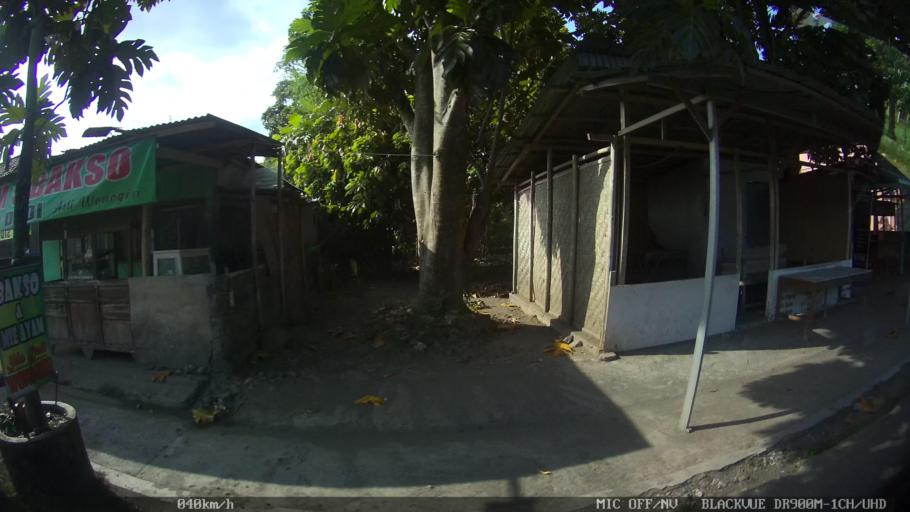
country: ID
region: Central Java
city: Candi Prambanan
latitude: -7.7292
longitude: 110.4665
